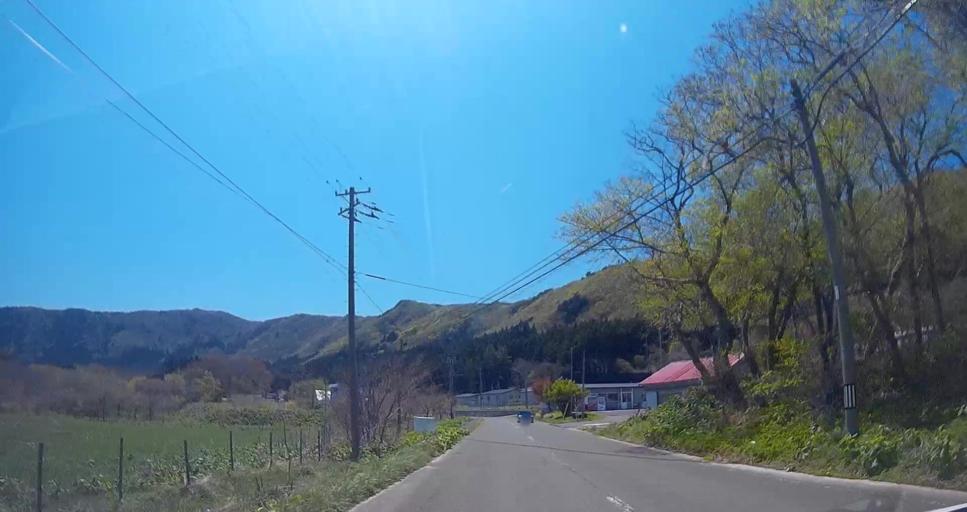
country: JP
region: Aomori
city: Mutsu
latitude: 41.4085
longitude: 141.4479
